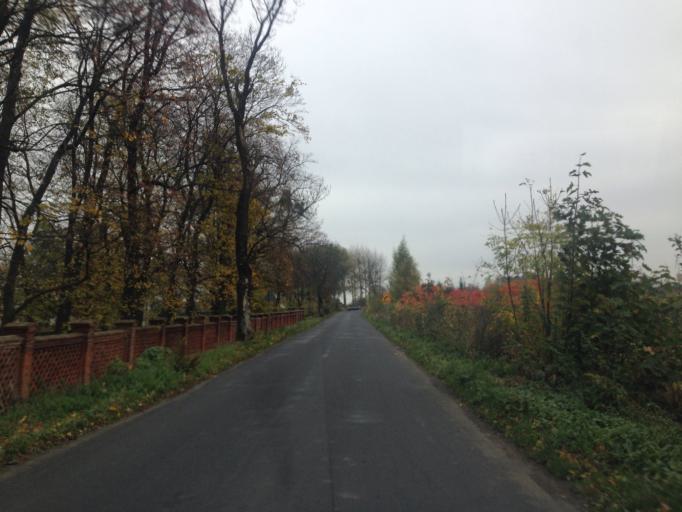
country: PL
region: Kujawsko-Pomorskie
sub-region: Powiat grudziadzki
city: Radzyn Chelminski
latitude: 53.3918
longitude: 18.8356
